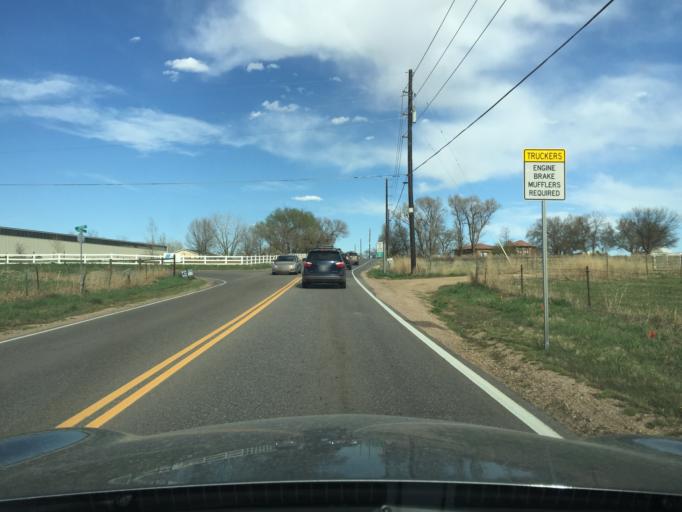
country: US
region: Colorado
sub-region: Boulder County
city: Lafayette
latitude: 40.0365
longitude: -105.0987
